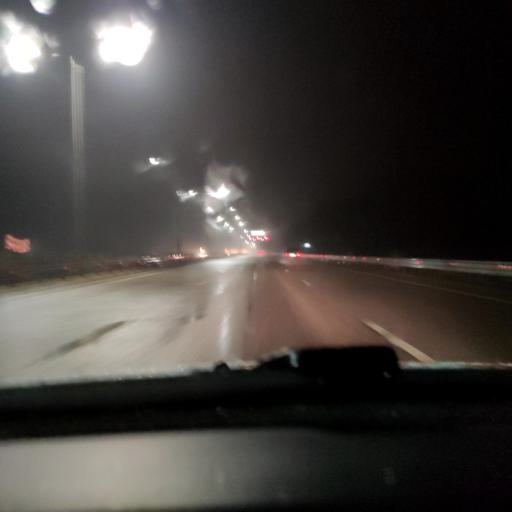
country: RU
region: Voronezj
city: Somovo
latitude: 51.6999
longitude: 39.3048
